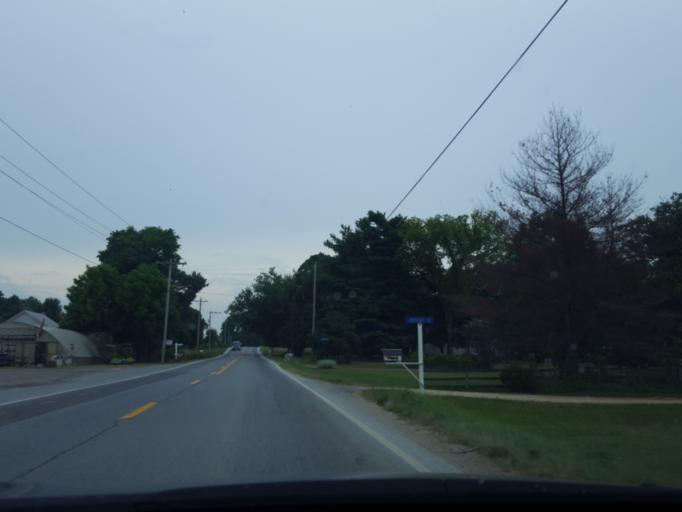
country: US
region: Maryland
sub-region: Saint Mary's County
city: Charlotte Hall
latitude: 38.4539
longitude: -76.7841
